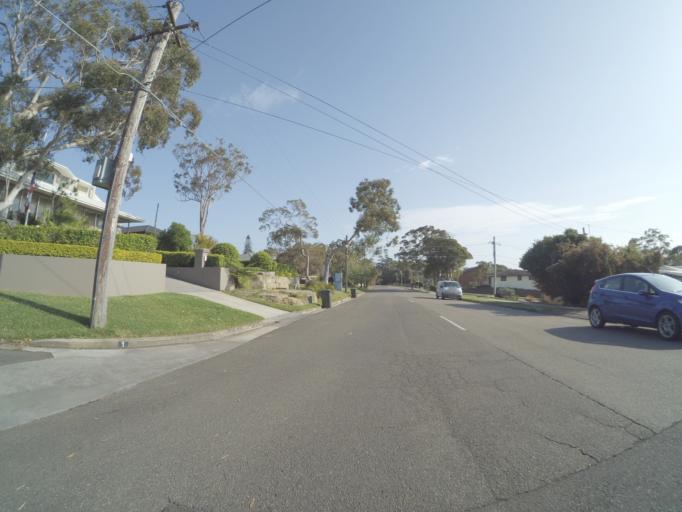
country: AU
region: New South Wales
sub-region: Sutherland Shire
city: Dolans Bay
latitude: -34.0705
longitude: 151.1378
